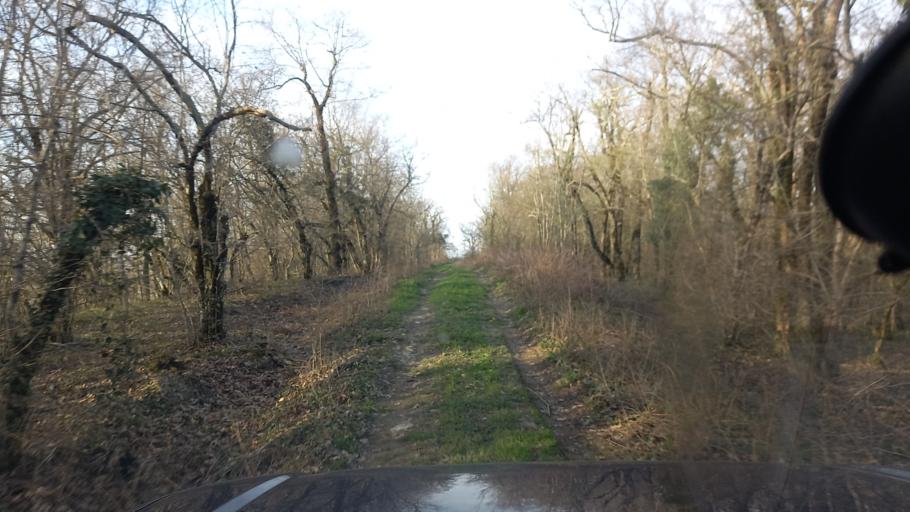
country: RU
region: Krasnodarskiy
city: Arkhipo-Osipovka
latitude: 44.3585
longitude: 38.5527
